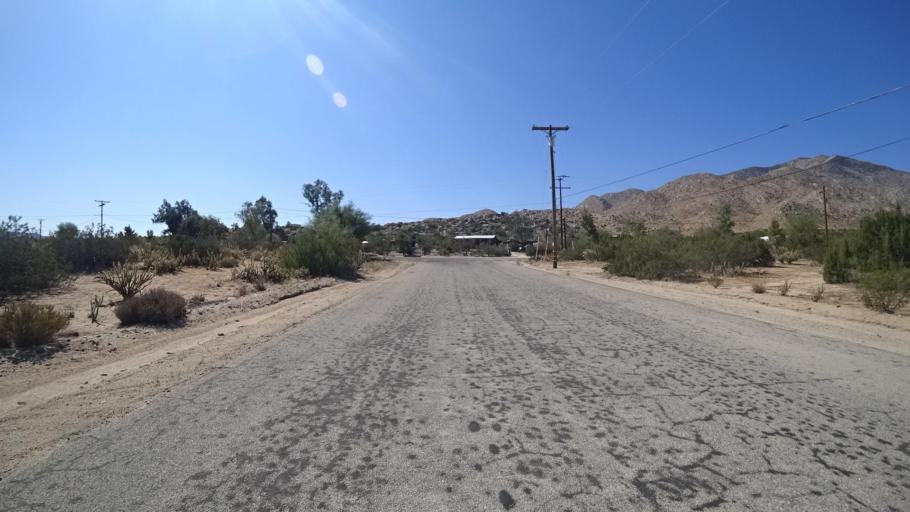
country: US
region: California
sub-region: San Diego County
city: Julian
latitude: 33.0752
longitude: -116.4444
